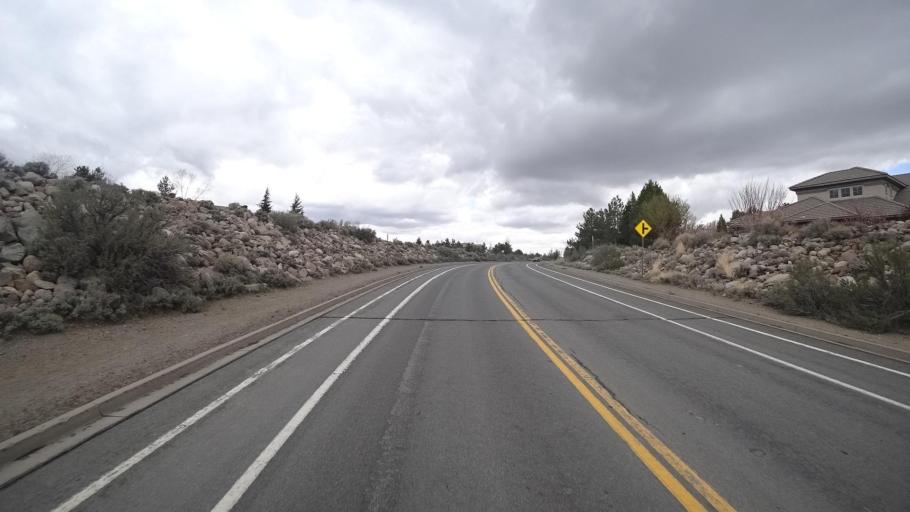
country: US
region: Nevada
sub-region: Washoe County
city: Reno
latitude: 39.3949
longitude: -119.7919
